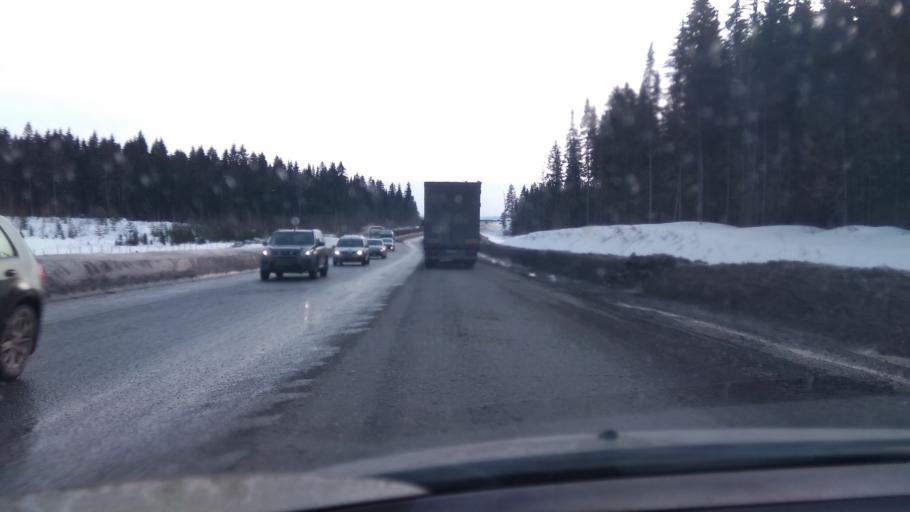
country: RU
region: Perm
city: Ferma
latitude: 57.9468
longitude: 56.3845
